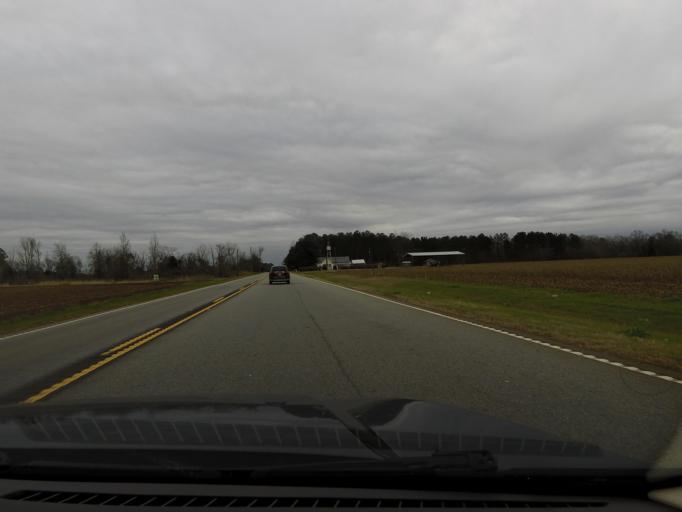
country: US
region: Georgia
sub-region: Randolph County
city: Shellman
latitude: 31.7704
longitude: -84.5382
